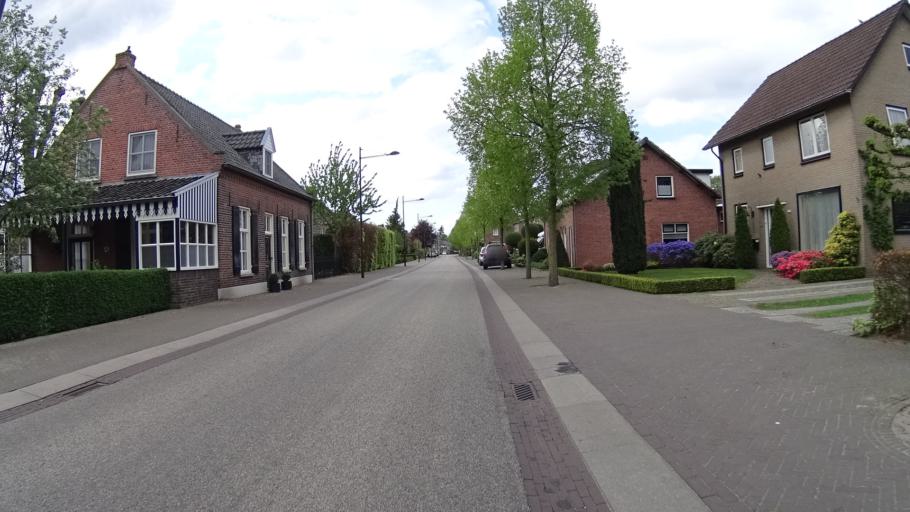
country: NL
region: North Brabant
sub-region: Gemeente Boekel
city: Boekel
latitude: 51.5816
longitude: 5.7118
